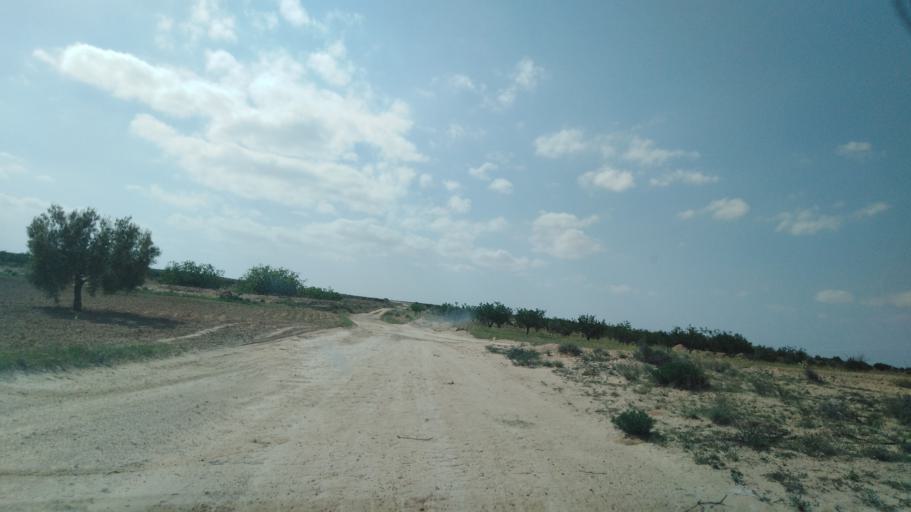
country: TN
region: Safaqis
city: Bi'r `Ali Bin Khalifah
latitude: 34.8004
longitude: 10.3802
